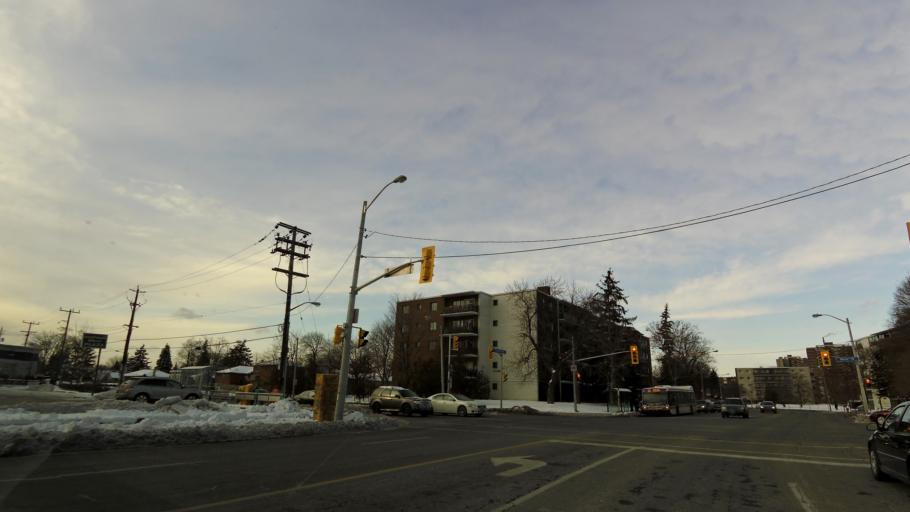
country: CA
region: Ontario
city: Etobicoke
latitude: 43.6354
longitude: -79.5621
